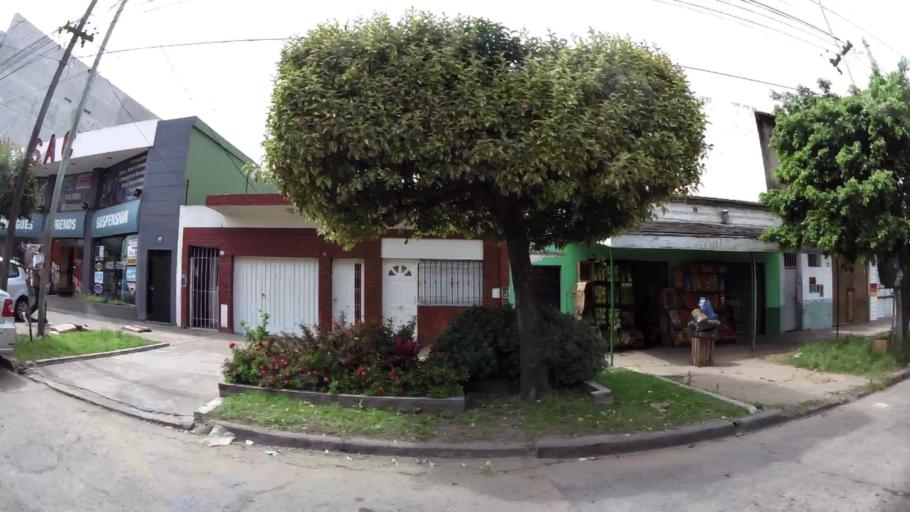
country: AR
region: Buenos Aires F.D.
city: Villa Lugano
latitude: -34.6905
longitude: -58.4984
